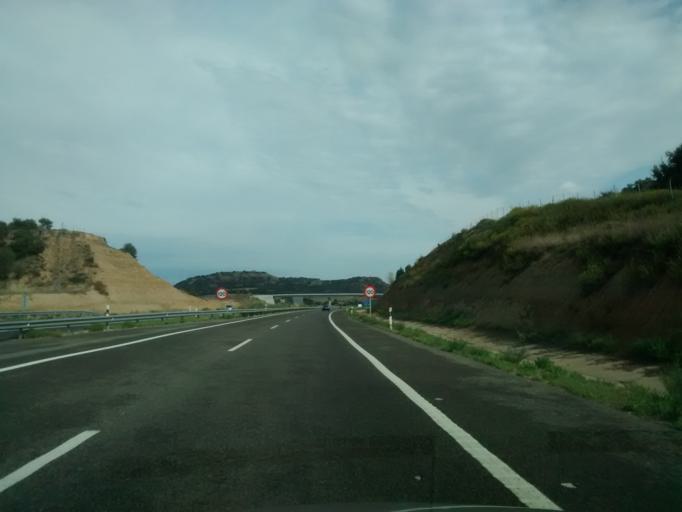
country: ES
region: Aragon
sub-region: Provincia de Huesca
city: Ibieca
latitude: 42.1146
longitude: -0.2255
